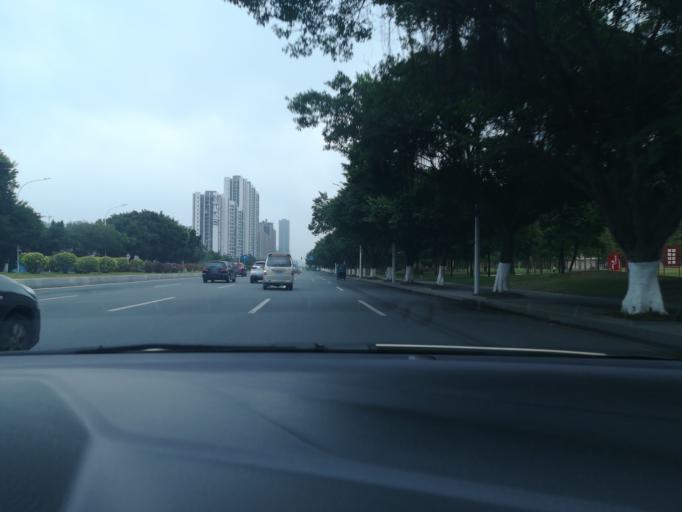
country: CN
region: Guangdong
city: Nansha
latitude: 22.8006
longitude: 113.5595
